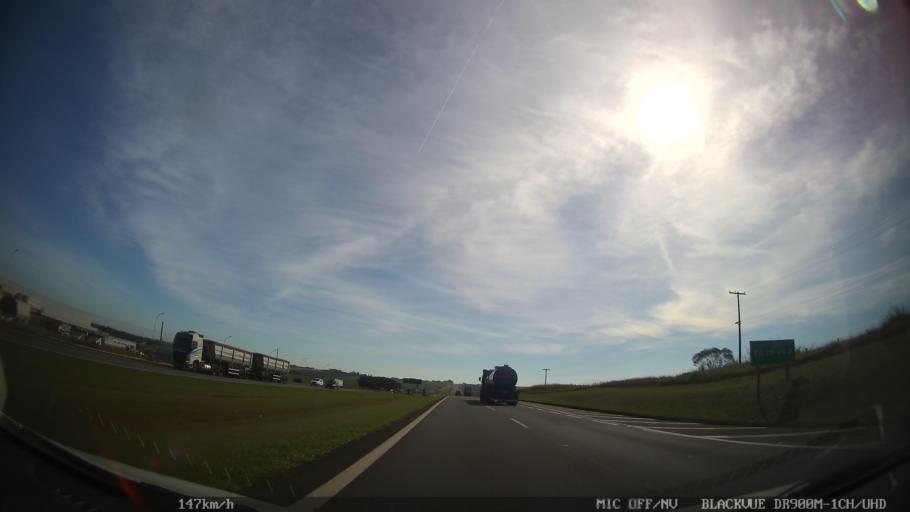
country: BR
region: Sao Paulo
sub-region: Cordeiropolis
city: Cordeiropolis
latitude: -22.4926
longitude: -47.3991
